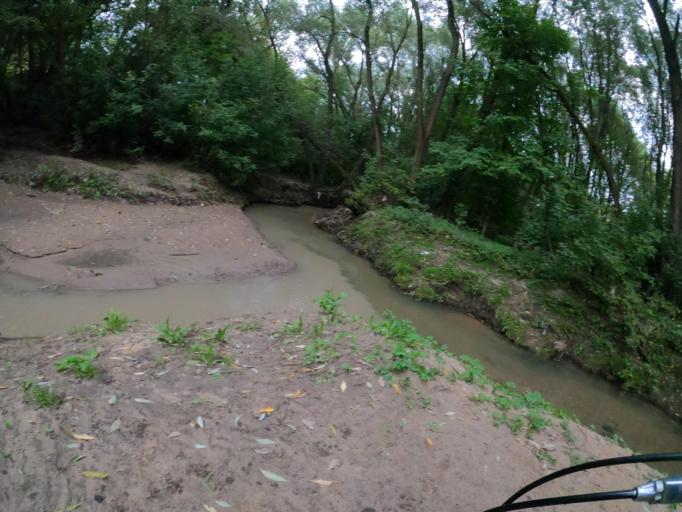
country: RU
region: Moscow
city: Tsaritsyno
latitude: 55.6154
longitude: 37.6513
